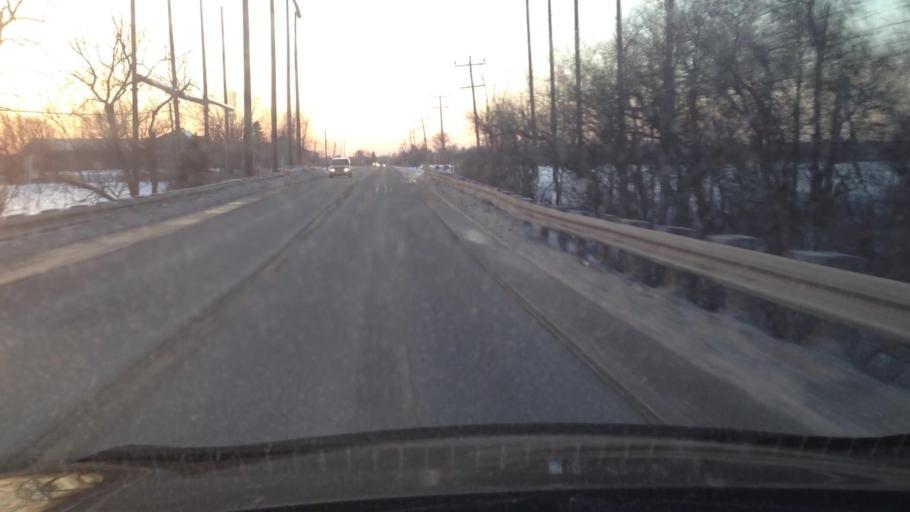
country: CA
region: Quebec
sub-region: Laurentides
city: Sainte-Sophie
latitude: 45.8365
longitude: -73.8439
